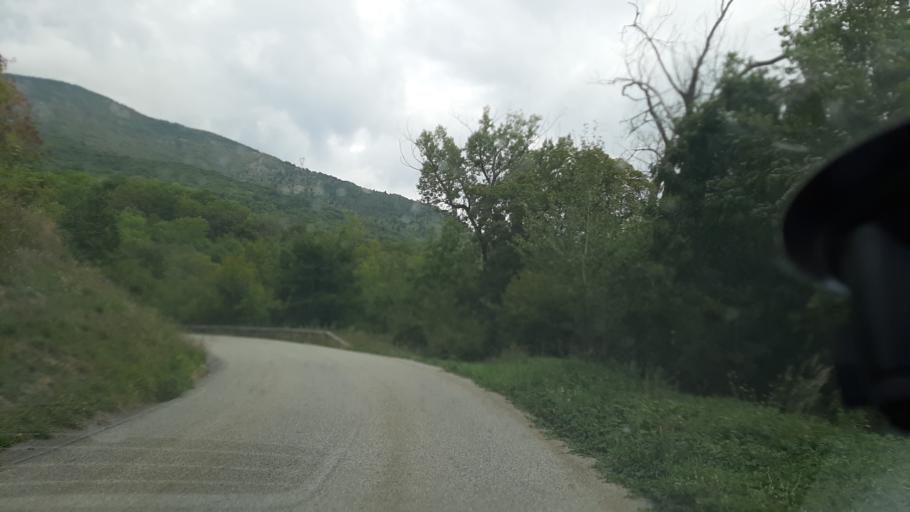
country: FR
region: Rhone-Alpes
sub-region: Departement de la Savoie
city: Saint-Michel-de-Maurienne
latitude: 45.2316
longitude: 6.4613
